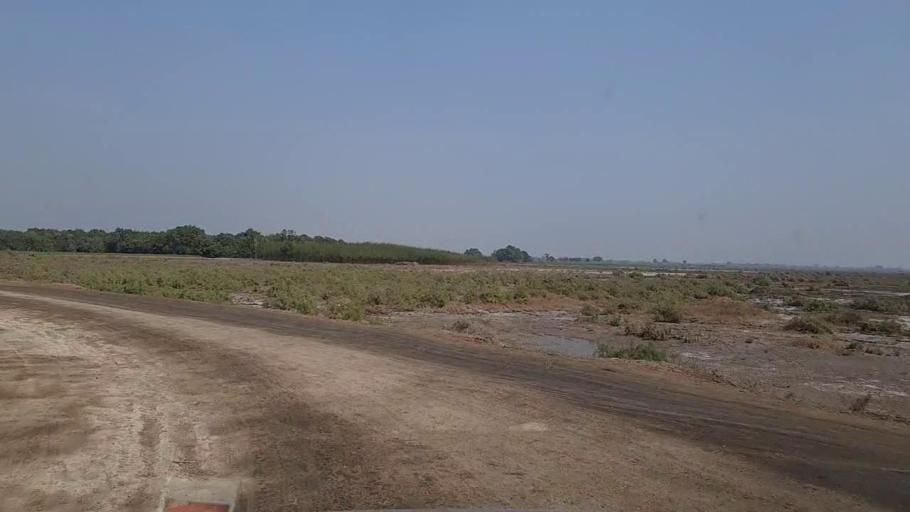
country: PK
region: Sindh
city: Mirwah Gorchani
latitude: 25.3369
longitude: 69.0635
